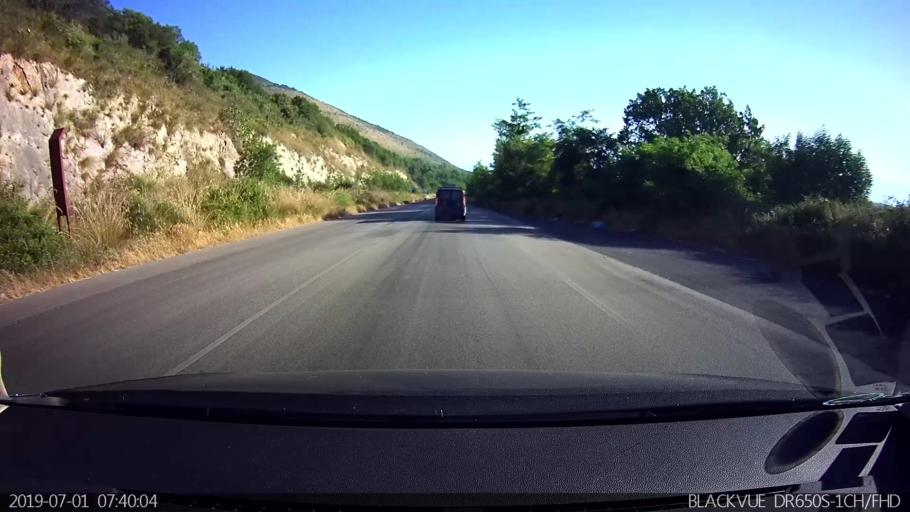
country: IT
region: Latium
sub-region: Provincia di Frosinone
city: Giuliano di Roma
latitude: 41.5546
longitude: 13.2666
